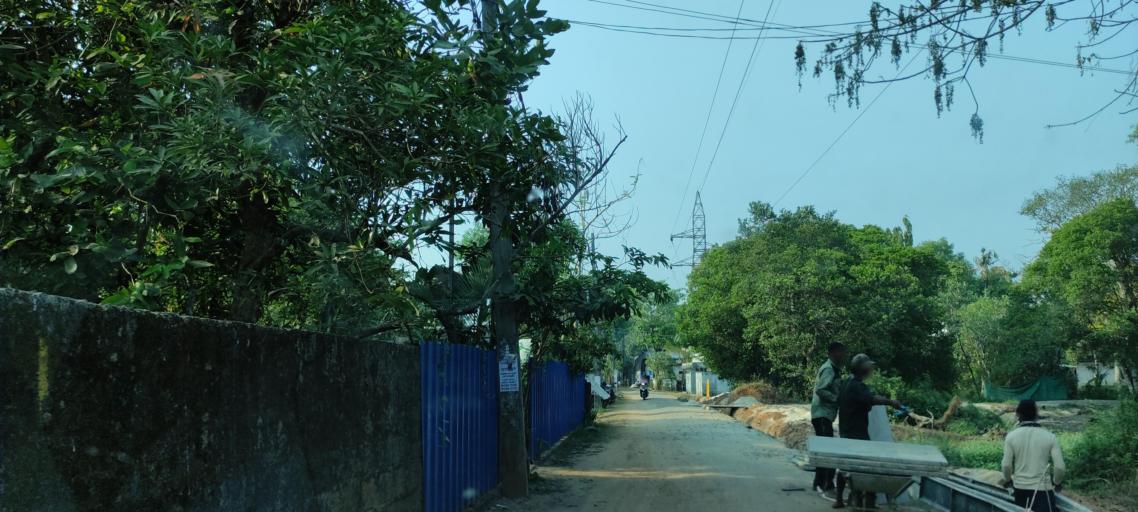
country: IN
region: Kerala
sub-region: Alappuzha
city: Alleppey
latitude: 9.5257
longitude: 76.3217
